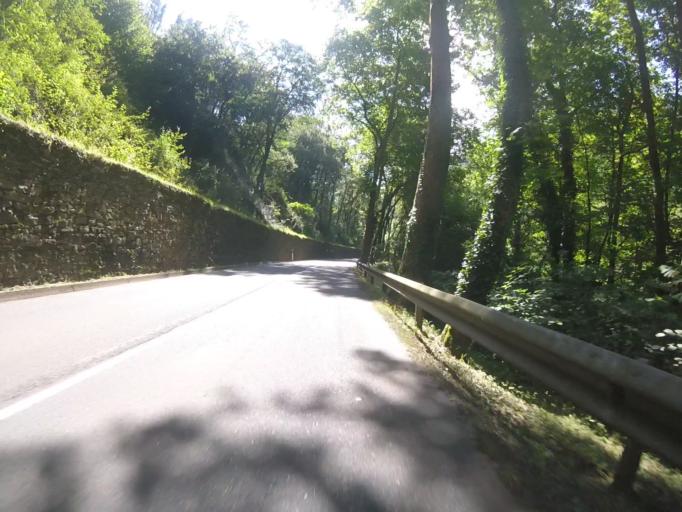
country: ES
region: Basque Country
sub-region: Provincia de Guipuzcoa
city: Azpeitia
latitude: 43.1793
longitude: -2.2421
